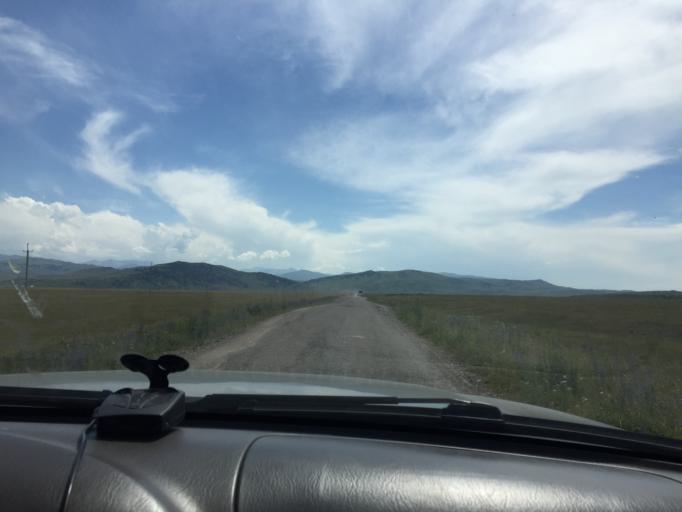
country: KZ
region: Almaty Oblysy
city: Kegen
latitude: 42.7986
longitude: 79.1786
